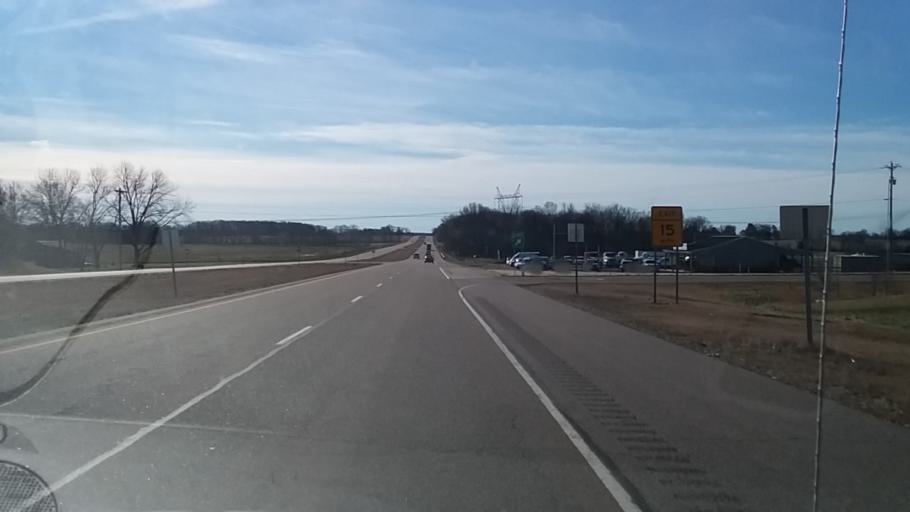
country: US
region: Tennessee
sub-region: Crockett County
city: Alamo
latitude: 35.8822
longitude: -89.2271
